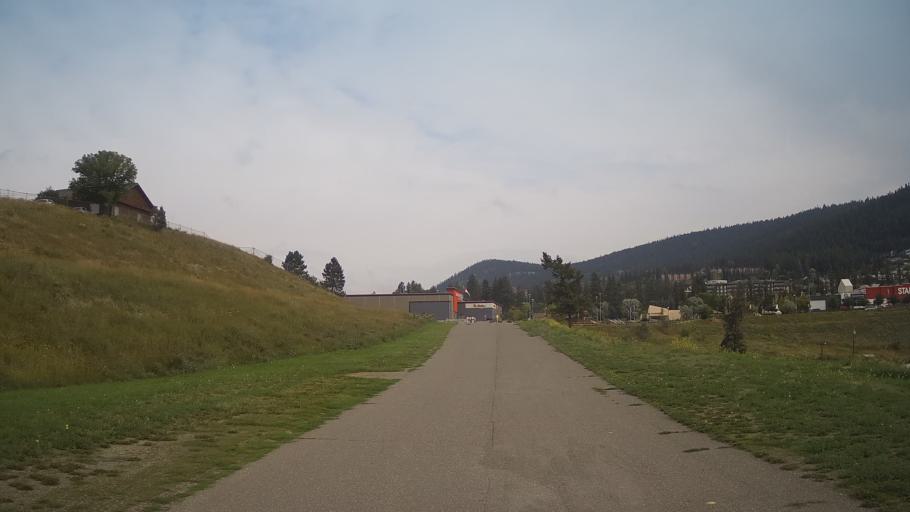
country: CA
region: British Columbia
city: Williams Lake
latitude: 52.1262
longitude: -122.1340
